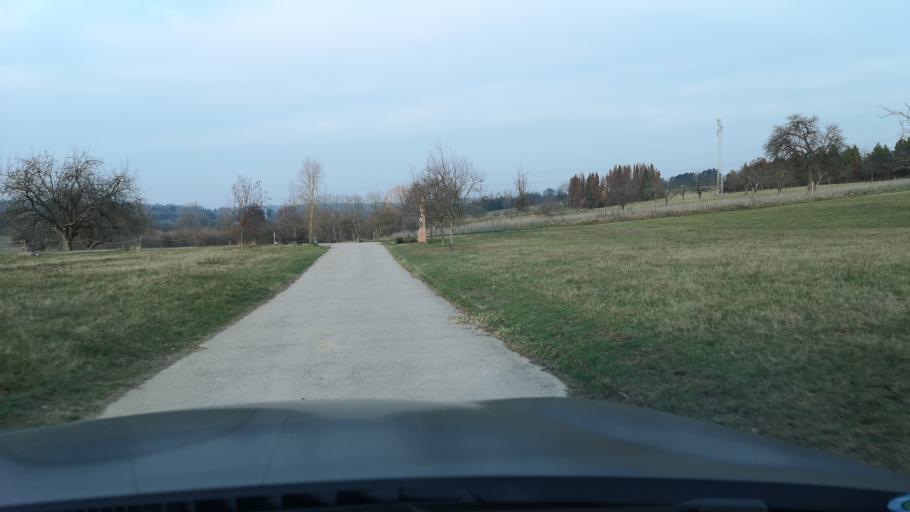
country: DE
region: Baden-Wuerttemberg
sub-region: Karlsruhe Region
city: Ettlingen
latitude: 48.9376
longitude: 8.4677
